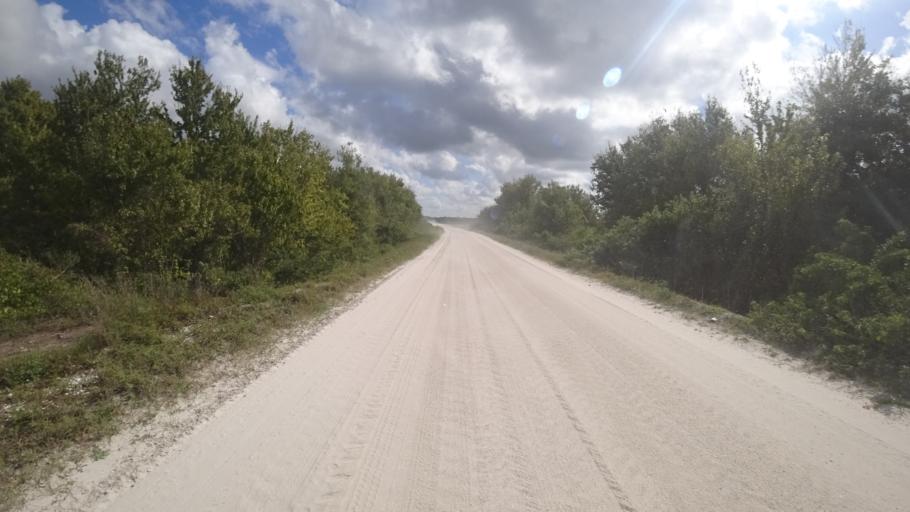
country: US
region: Florida
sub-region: Sarasota County
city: Lake Sarasota
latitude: 27.4131
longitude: -82.1974
